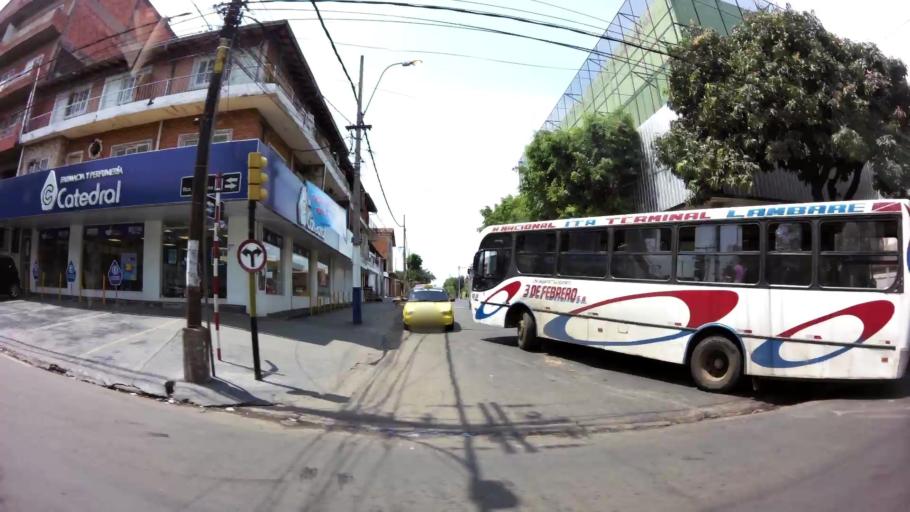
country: PY
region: Central
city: Lambare
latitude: -25.3217
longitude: -57.5942
